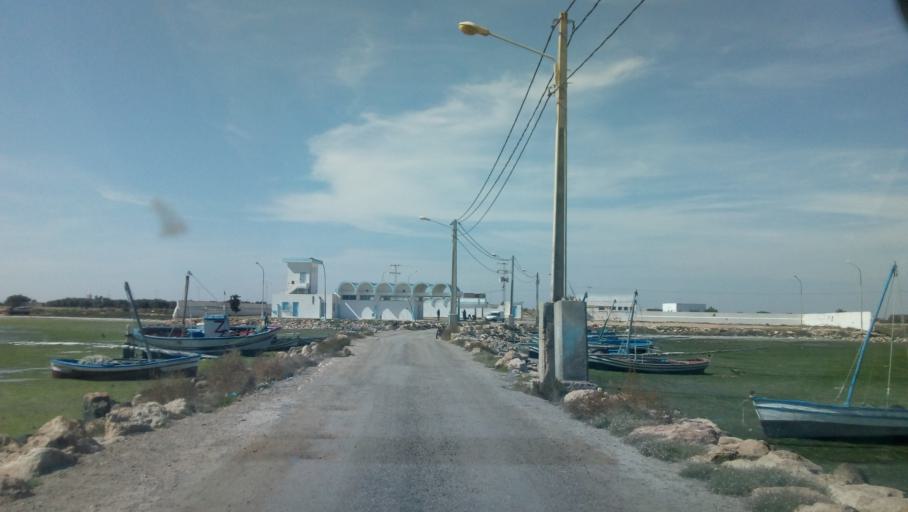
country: TN
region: Safaqis
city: Jabinyanah
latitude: 34.8703
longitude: 10.9102
